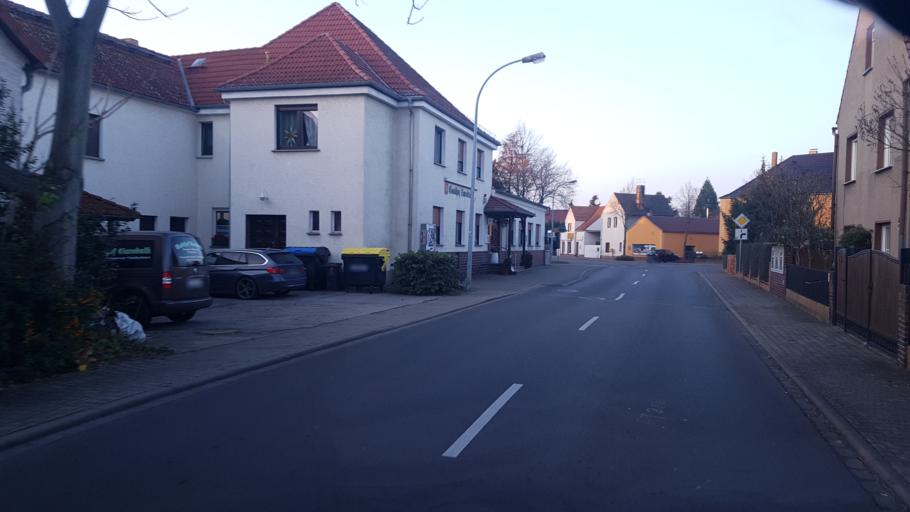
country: DE
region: Brandenburg
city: Tettau
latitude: 51.4314
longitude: 13.7275
